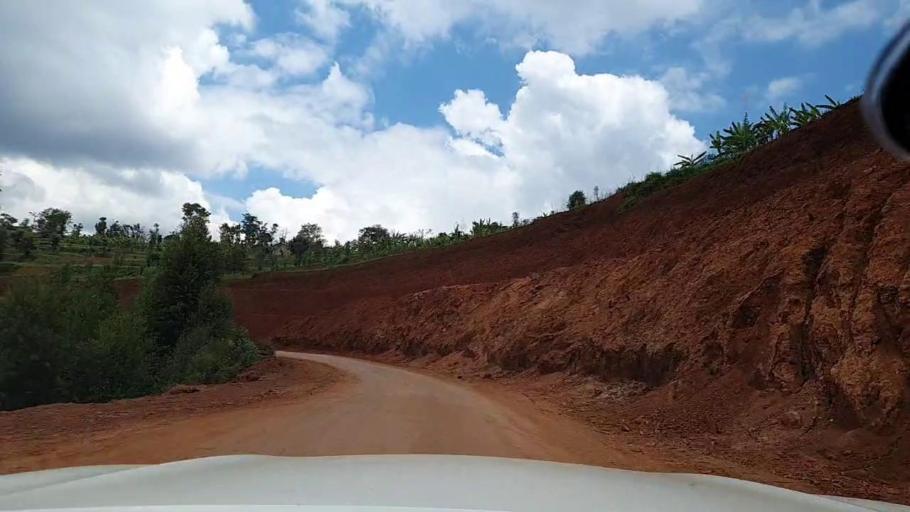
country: RW
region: Southern Province
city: Butare
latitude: -2.7074
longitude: 29.5504
